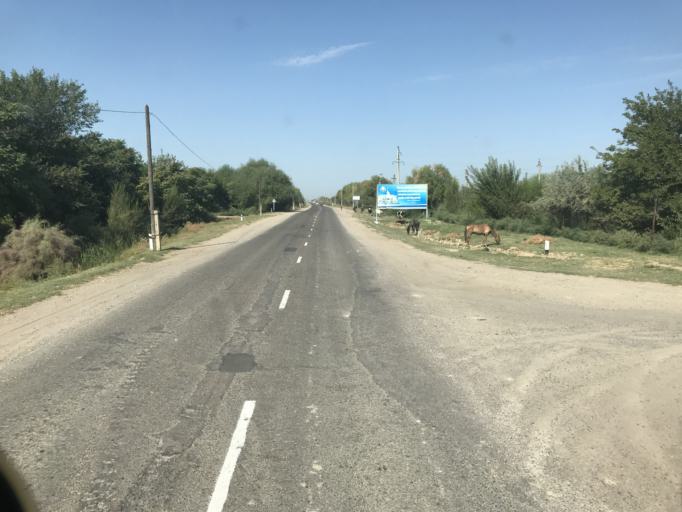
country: KZ
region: Ongtustik Qazaqstan
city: Myrzakent
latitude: 40.6851
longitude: 68.5918
